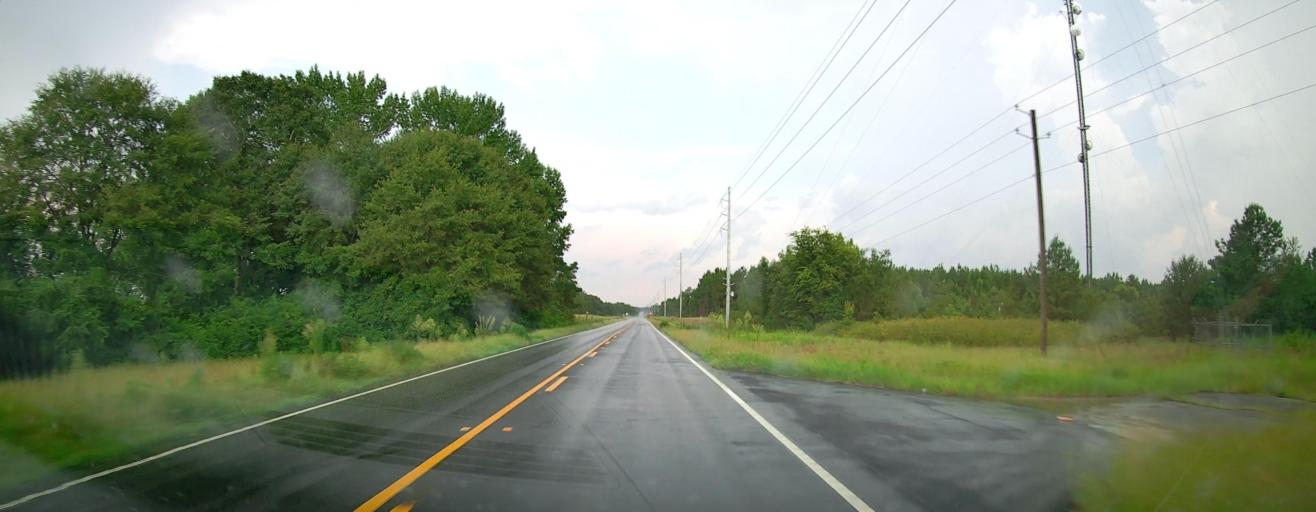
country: US
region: Georgia
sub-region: Dodge County
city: Chester
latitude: 32.5711
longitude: -83.1904
